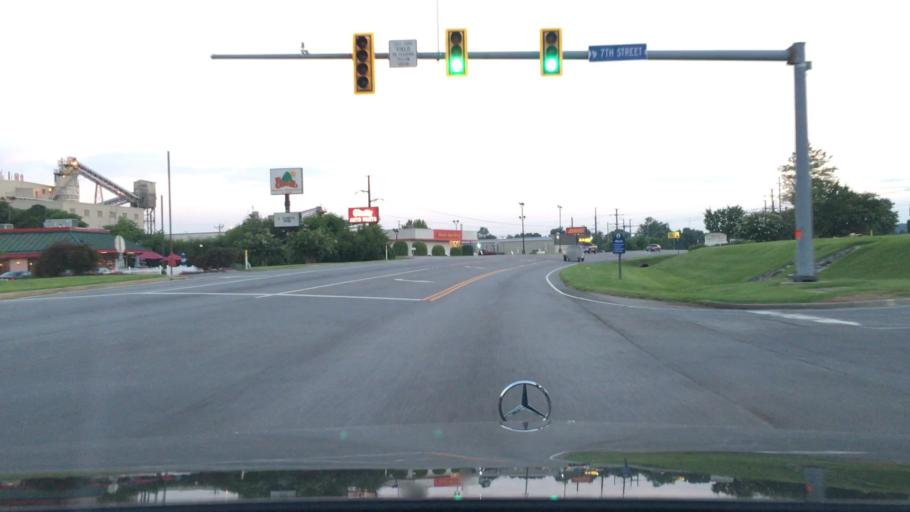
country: US
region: Virginia
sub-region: Campbell County
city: Altavista
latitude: 37.1209
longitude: -79.2742
